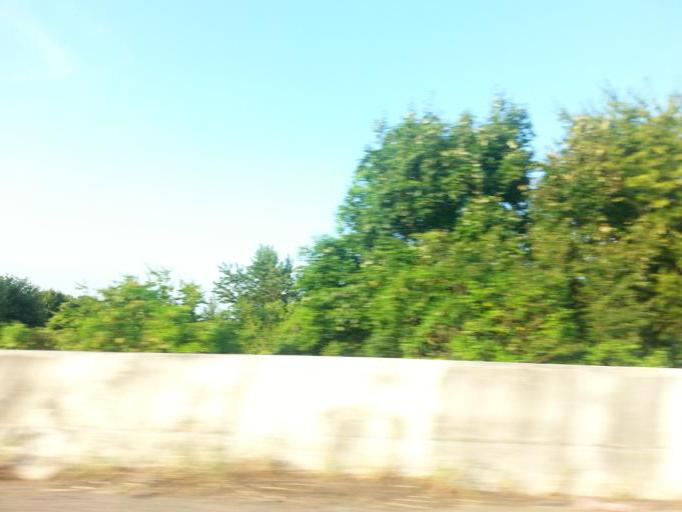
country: US
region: Tennessee
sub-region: McMinn County
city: Athens
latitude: 35.4784
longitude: -84.5896
